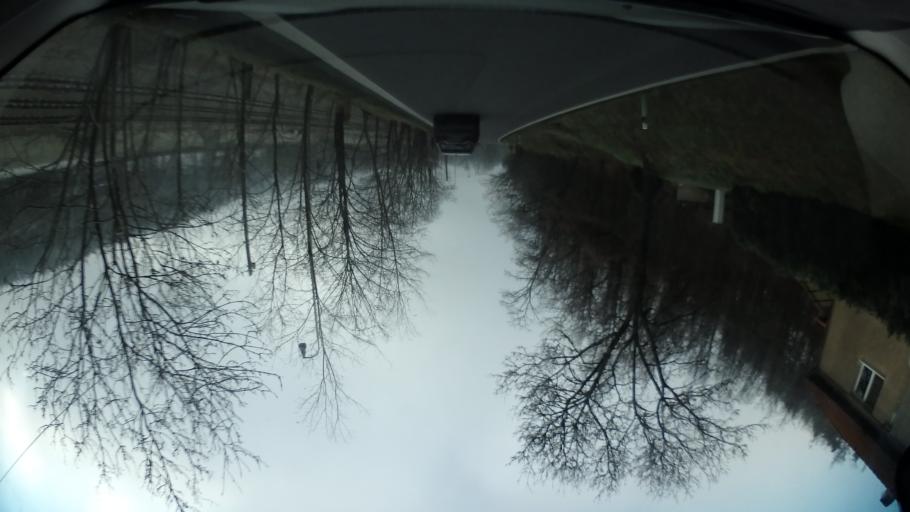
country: CZ
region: Vysocina
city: Vladislav
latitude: 49.2128
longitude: 15.9670
